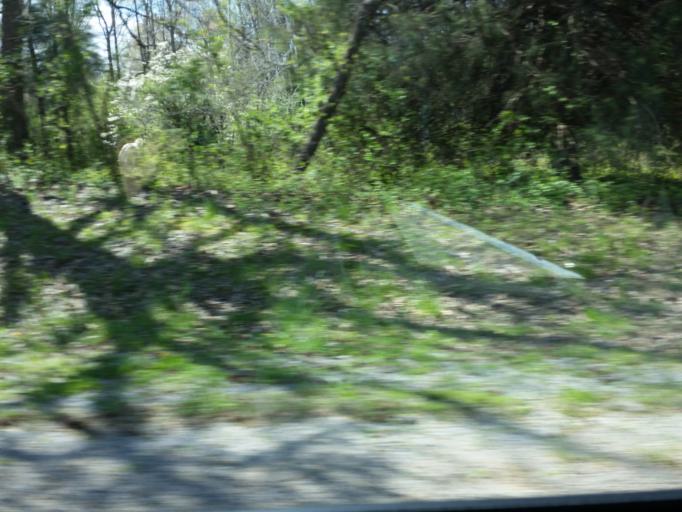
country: US
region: Arkansas
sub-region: Craighead County
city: Bono
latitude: 35.9439
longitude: -90.7116
